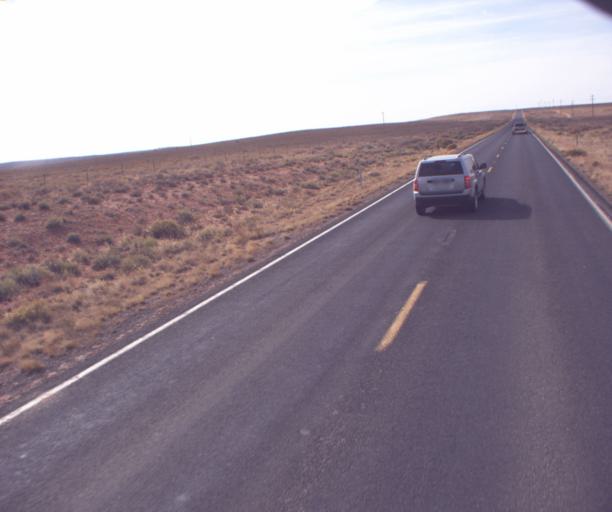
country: US
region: Arizona
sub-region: Apache County
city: Ganado
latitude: 35.9270
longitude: -109.6040
